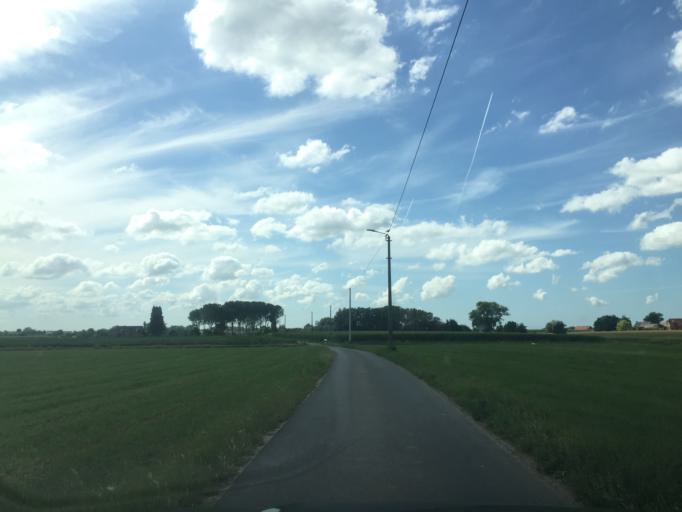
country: BE
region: Flanders
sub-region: Provincie West-Vlaanderen
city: Staden
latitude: 50.9851
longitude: 3.0374
